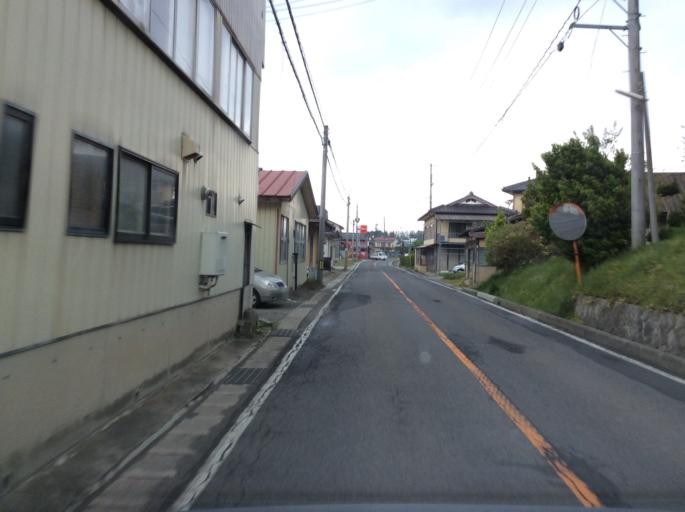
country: JP
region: Fukushima
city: Funehikimachi-funehiki
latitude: 37.3967
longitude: 140.5701
